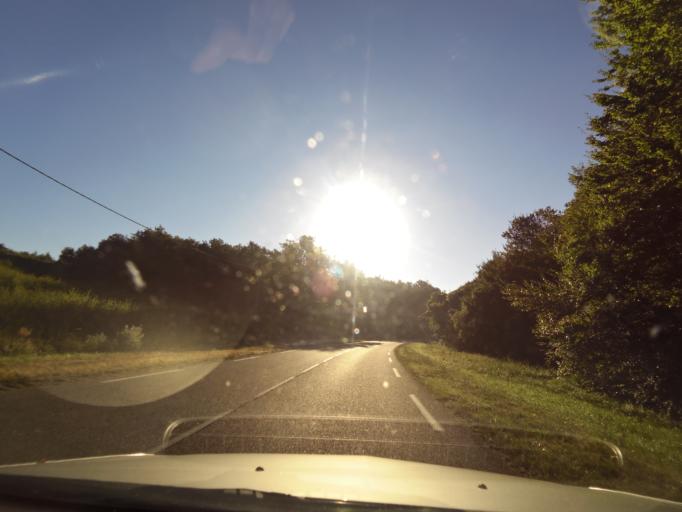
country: FR
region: Aquitaine
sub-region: Departement de la Gironde
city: Castets-en-Dorthe
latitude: 44.5069
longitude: -0.1552
